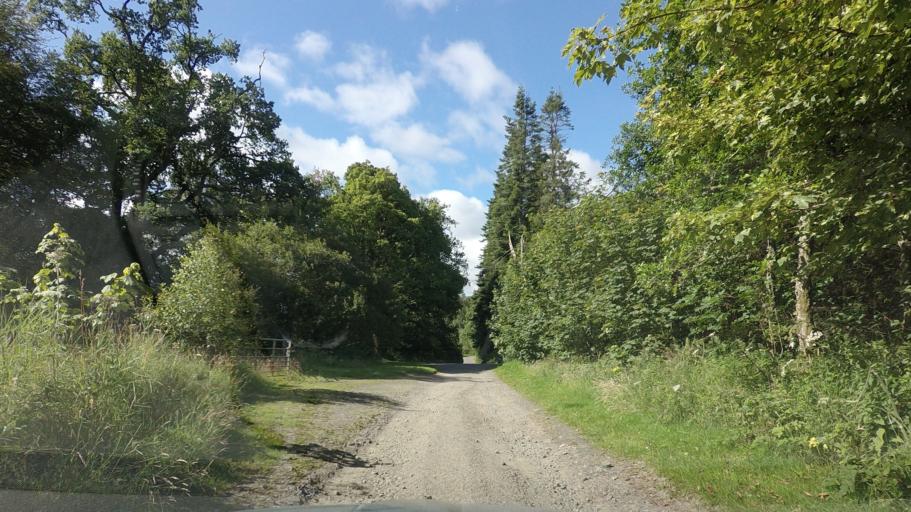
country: GB
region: Scotland
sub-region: Stirling
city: Killearn
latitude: 56.0691
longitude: -4.4788
